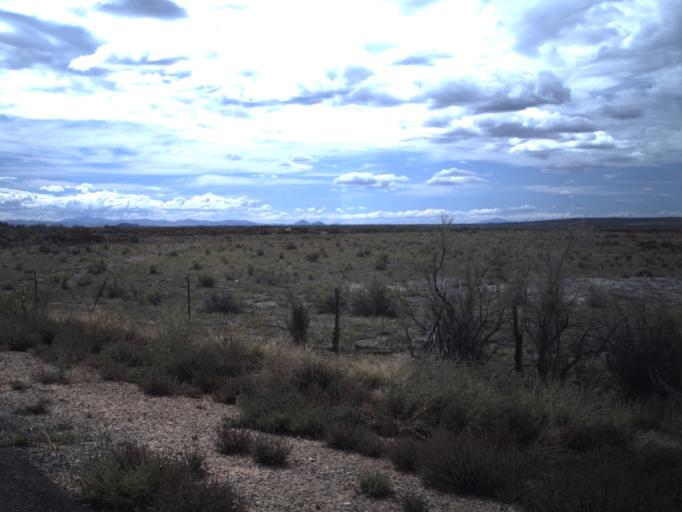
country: US
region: Utah
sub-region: Millard County
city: Fillmore
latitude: 39.1144
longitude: -112.4095
